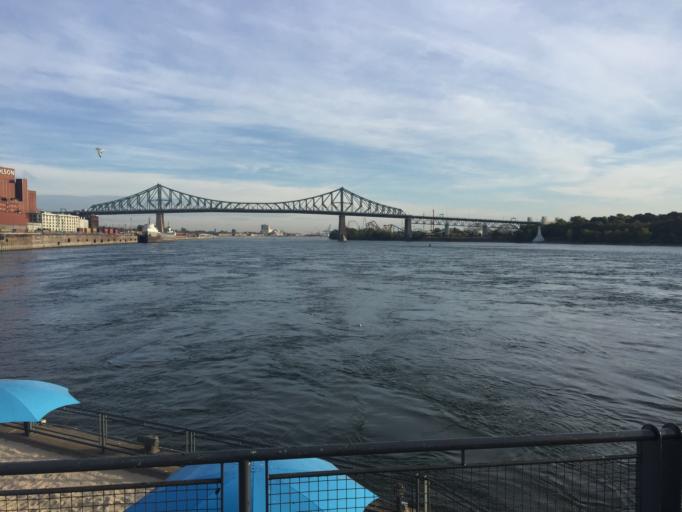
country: CA
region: Quebec
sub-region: Monteregie
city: Longueuil
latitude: 45.5123
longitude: -73.5457
